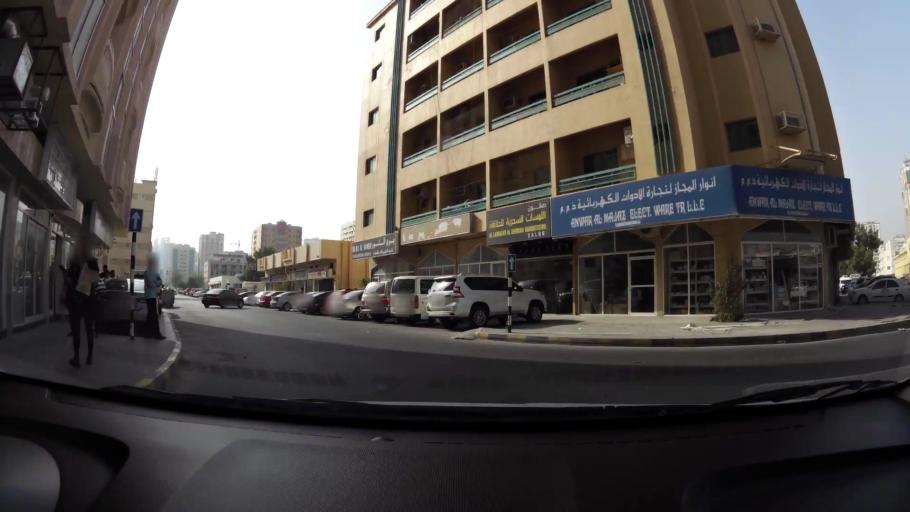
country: AE
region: Ash Shariqah
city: Sharjah
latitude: 25.3394
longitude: 55.3993
